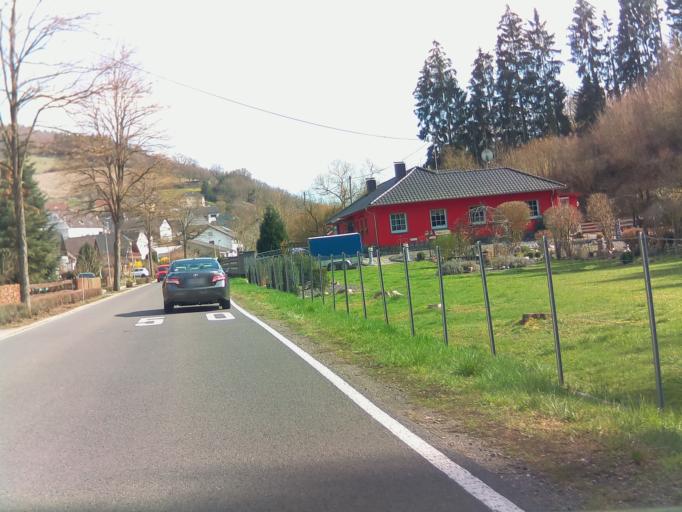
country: DE
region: Rheinland-Pfalz
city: Barenbach
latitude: 49.7507
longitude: 7.4366
